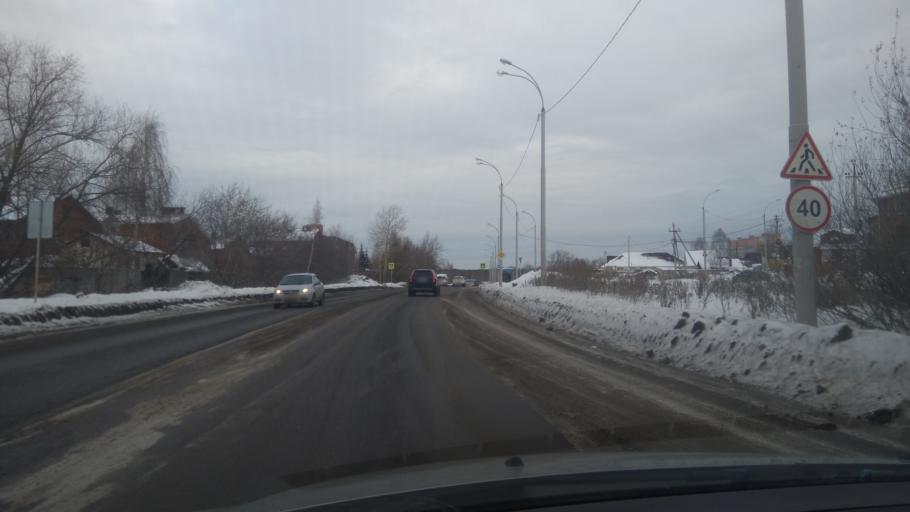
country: RU
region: Sverdlovsk
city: Shirokaya Rechka
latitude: 56.8053
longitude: 60.4949
